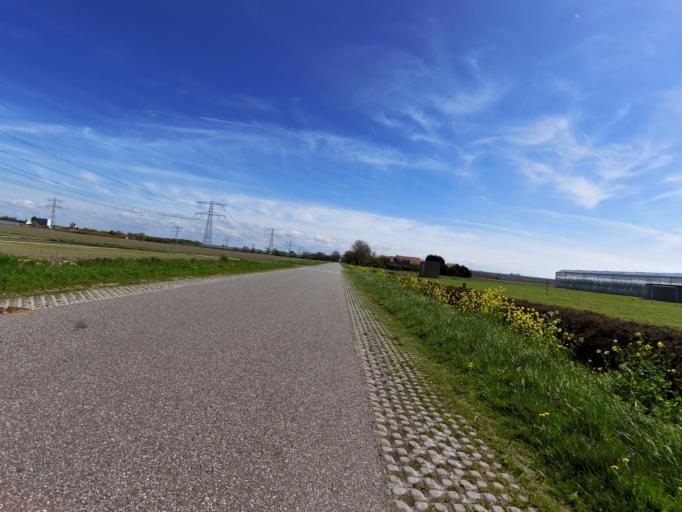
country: NL
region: South Holland
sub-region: Gemeente Brielle
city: Brielle
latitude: 51.9021
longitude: 4.1355
